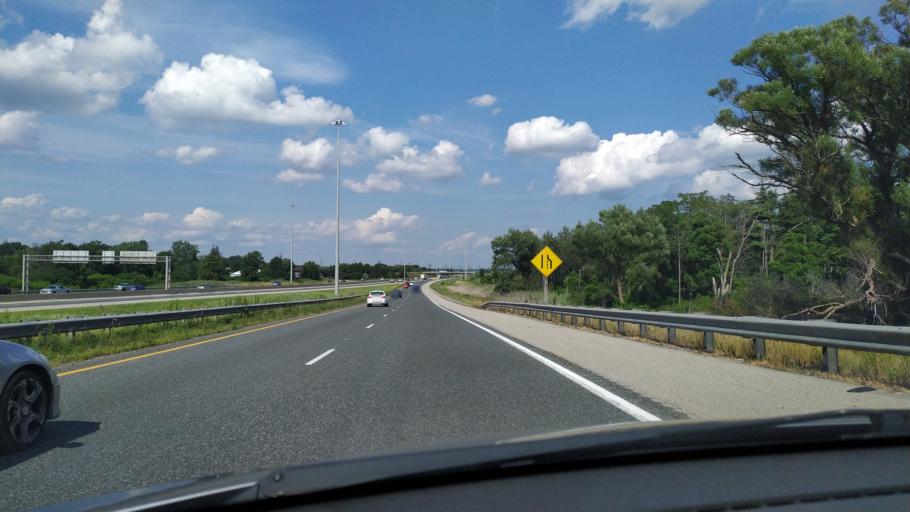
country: CA
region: Ontario
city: London
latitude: 42.9060
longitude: -81.2309
